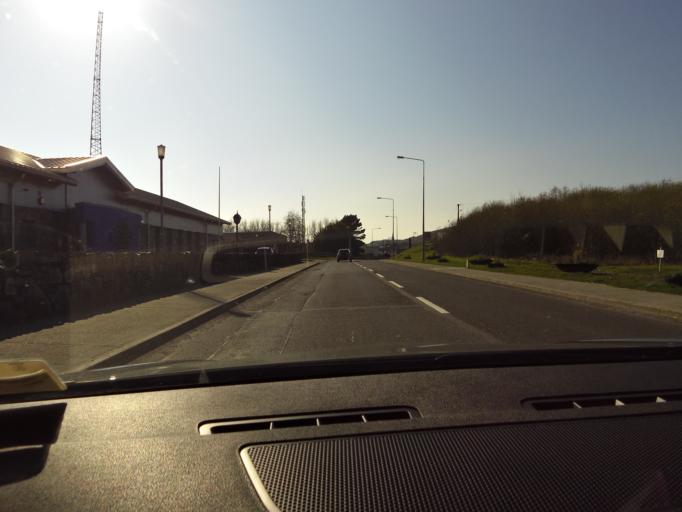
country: IE
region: Connaught
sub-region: County Galway
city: Clifden
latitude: 53.4884
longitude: -10.0086
